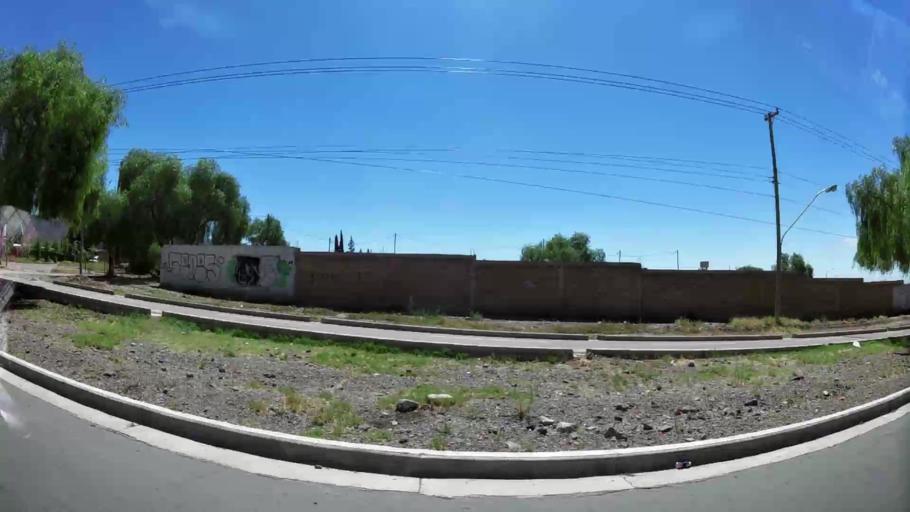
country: AR
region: Mendoza
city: Las Heras
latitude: -32.8536
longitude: -68.8666
